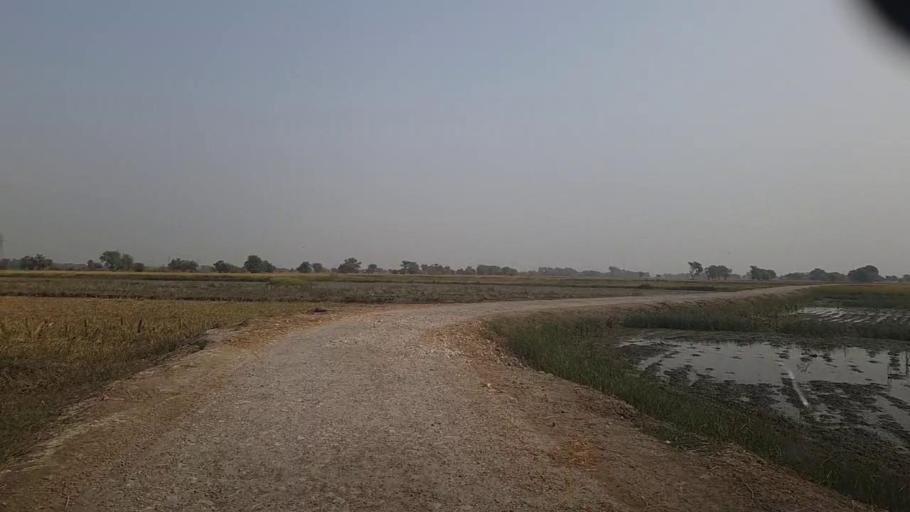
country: PK
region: Sindh
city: Kashmor
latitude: 28.3916
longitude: 69.4232
